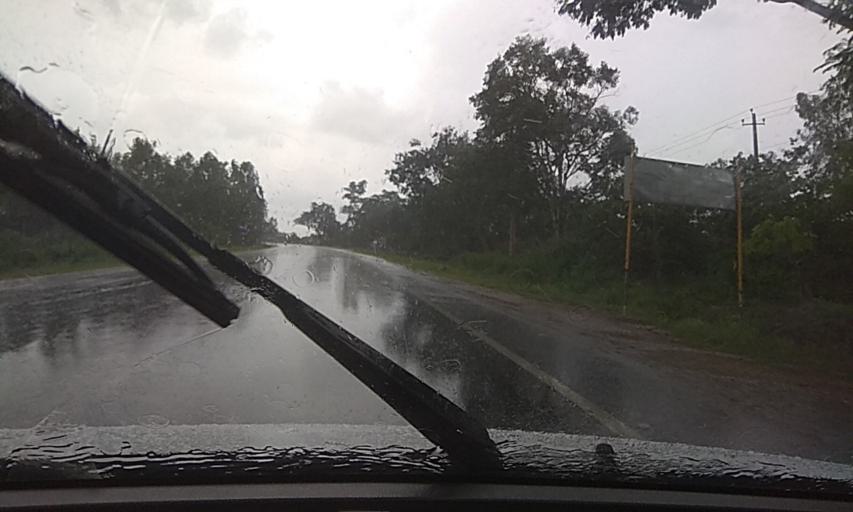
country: IN
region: Karnataka
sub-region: Tumkur
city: Kunigal
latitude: 12.9811
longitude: 77.0242
